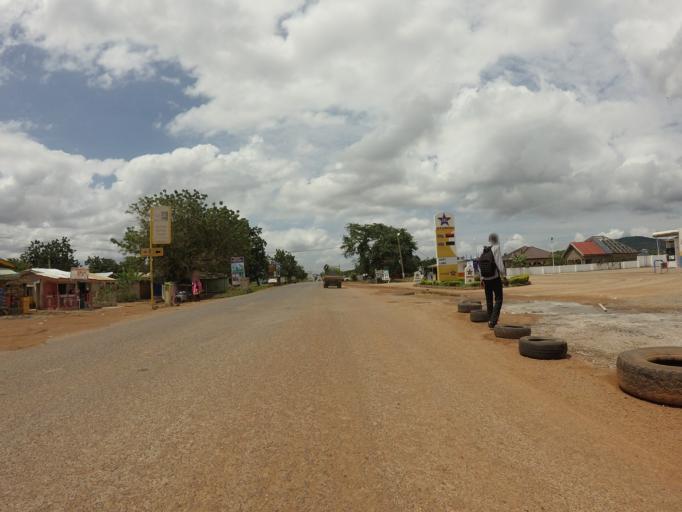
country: GH
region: Eastern
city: Aburi
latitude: 5.8371
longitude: -0.1166
